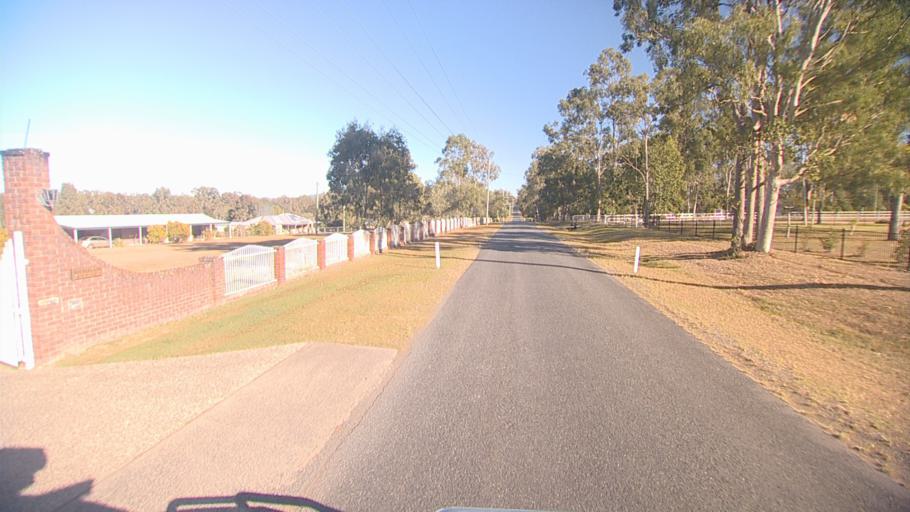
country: AU
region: Queensland
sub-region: Logan
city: North Maclean
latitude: -27.7883
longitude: 152.9708
